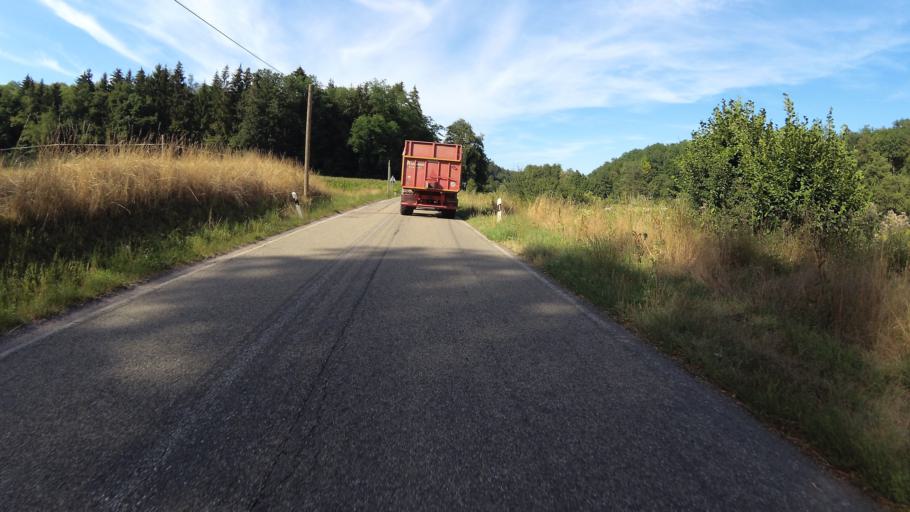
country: DE
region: Rheinland-Pfalz
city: Althornbach
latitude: 49.2013
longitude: 7.3288
